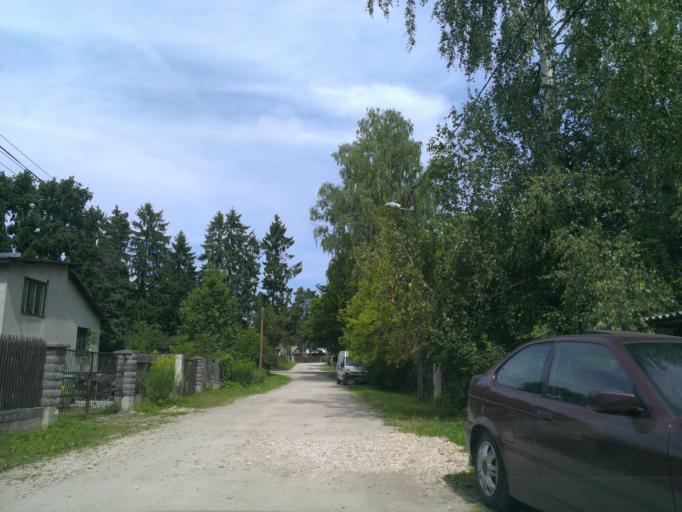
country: LV
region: Riga
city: Bergi
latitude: 56.9878
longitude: 24.2992
